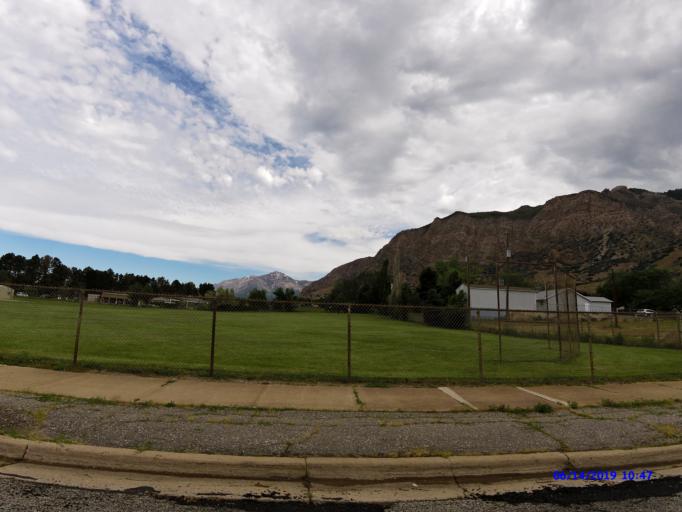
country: US
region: Utah
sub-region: Weber County
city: Ogden
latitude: 41.2483
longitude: -111.9431
